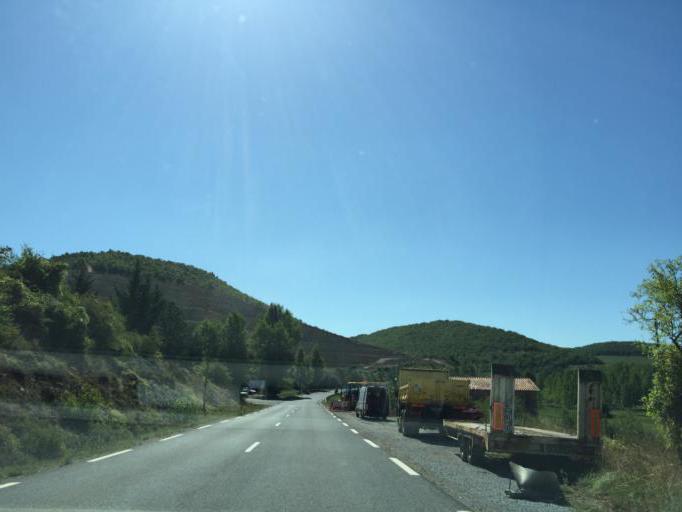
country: FR
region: Midi-Pyrenees
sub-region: Departement de l'Aveyron
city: Saint-Georges-de-Luzencon
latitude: 44.0387
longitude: 2.9158
